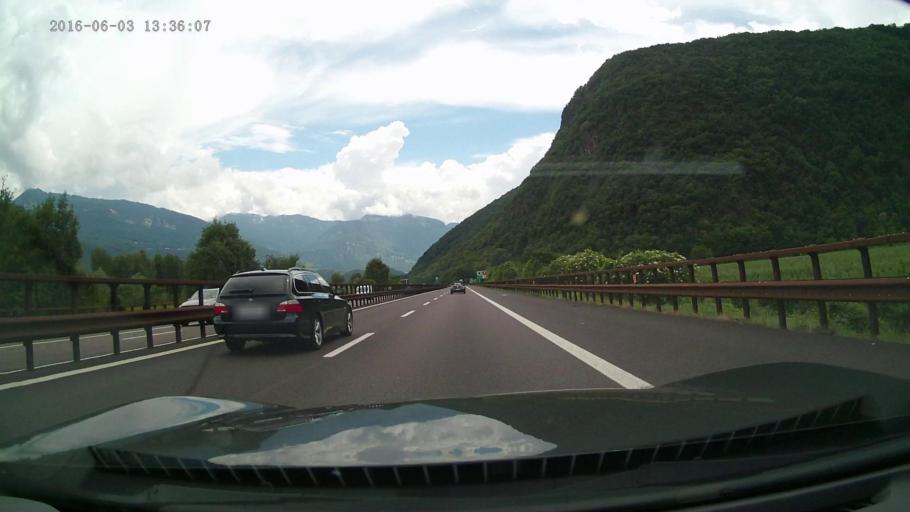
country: IT
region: Trentino-Alto Adige
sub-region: Bolzano
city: Ora
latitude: 46.3772
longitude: 11.2910
